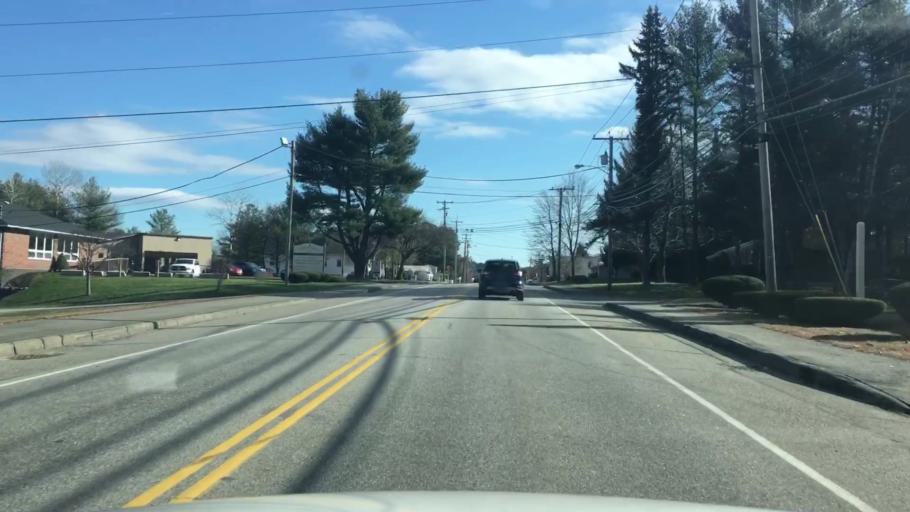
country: US
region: Maine
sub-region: Kennebec County
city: Augusta
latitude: 44.3071
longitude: -69.7515
